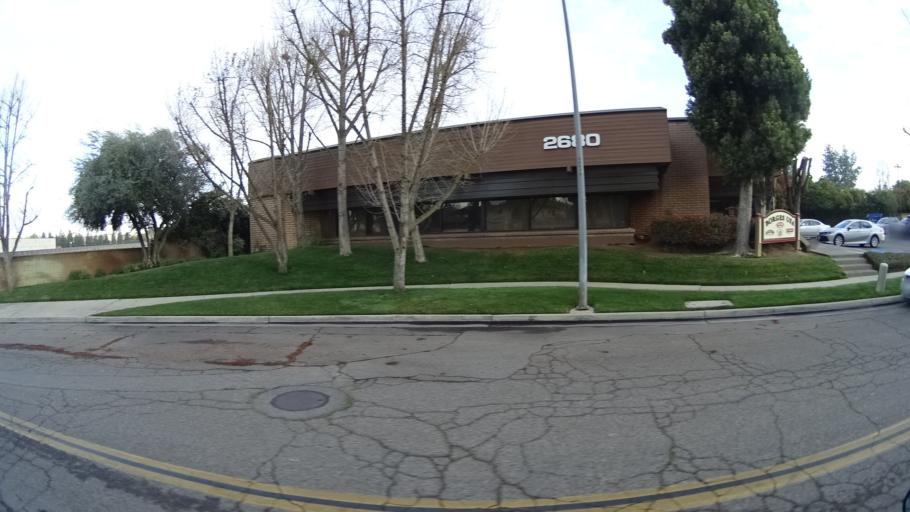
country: US
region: California
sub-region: Fresno County
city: Fresno
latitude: 36.8091
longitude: -119.8416
